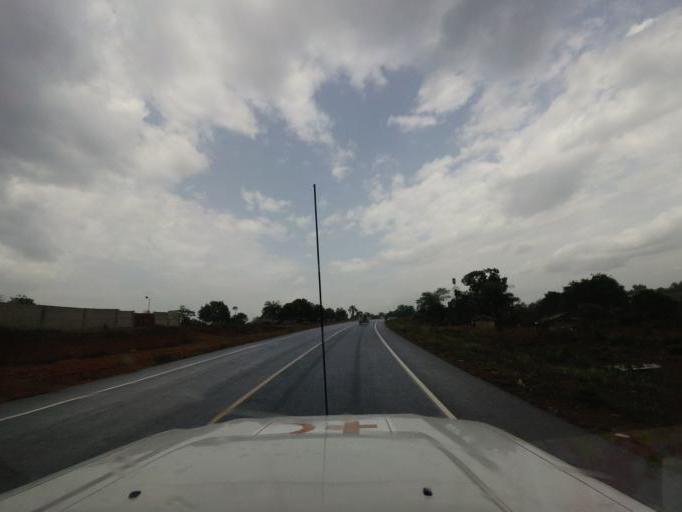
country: LR
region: Montserrado
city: Bensonville City
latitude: 6.4006
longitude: -10.5363
